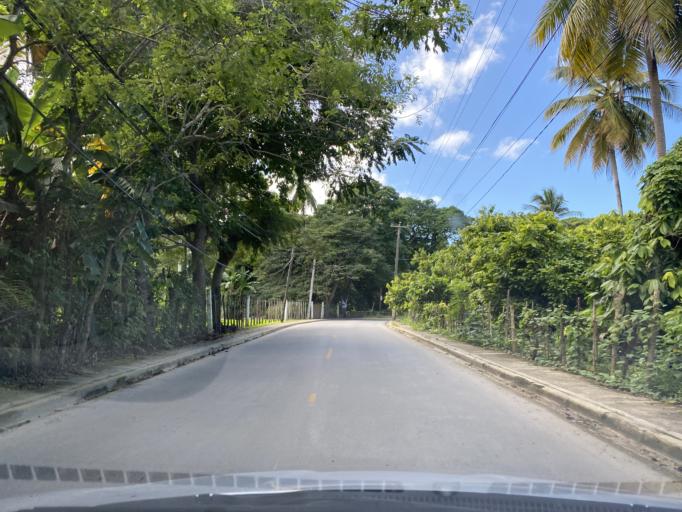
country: DO
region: Samana
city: Las Terrenas
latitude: 19.3059
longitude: -69.5607
